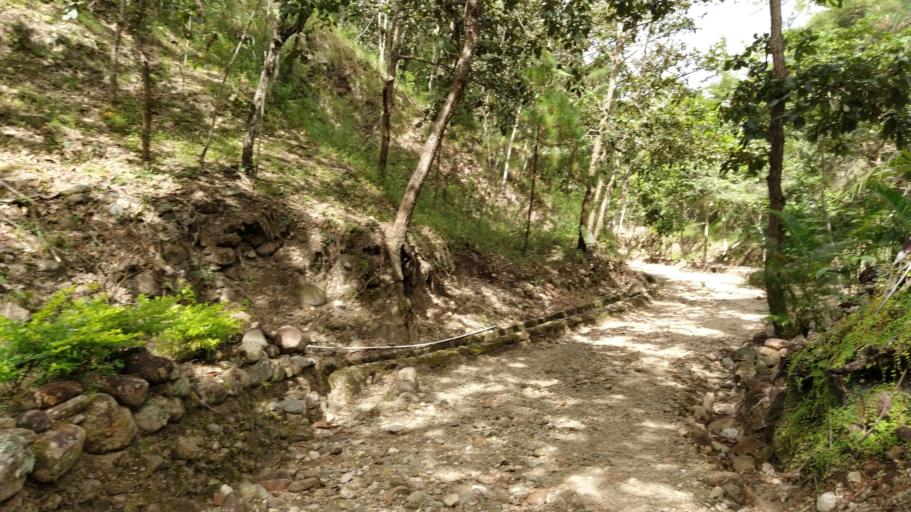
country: GT
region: Chiquimula
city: Esquipulas
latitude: 14.5572
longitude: -89.3172
